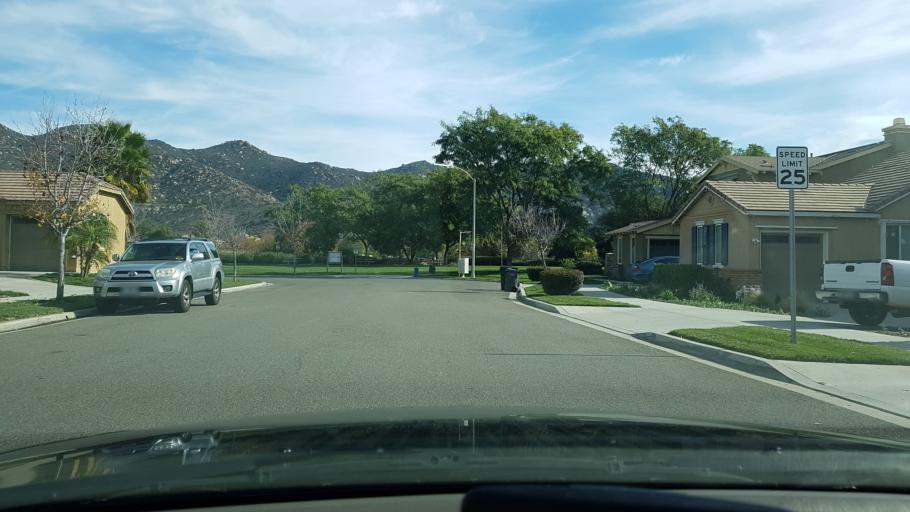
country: US
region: California
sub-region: San Diego County
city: Escondido
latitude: 33.1538
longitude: -117.0362
